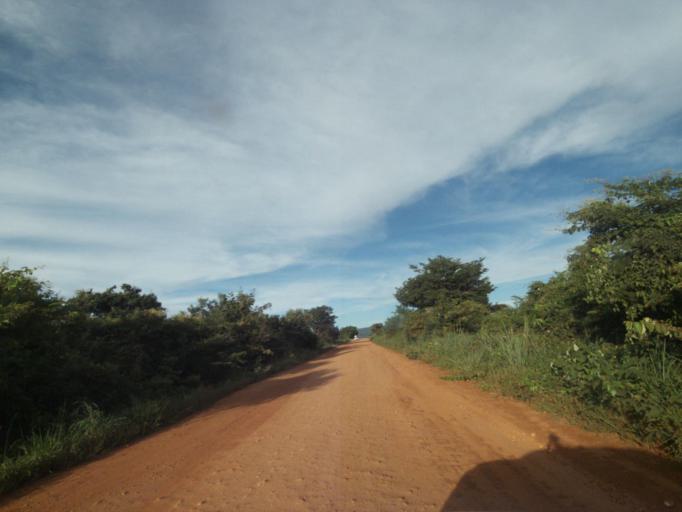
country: BR
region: Goias
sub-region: Jaragua
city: Jaragua
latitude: -15.8525
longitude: -49.3787
